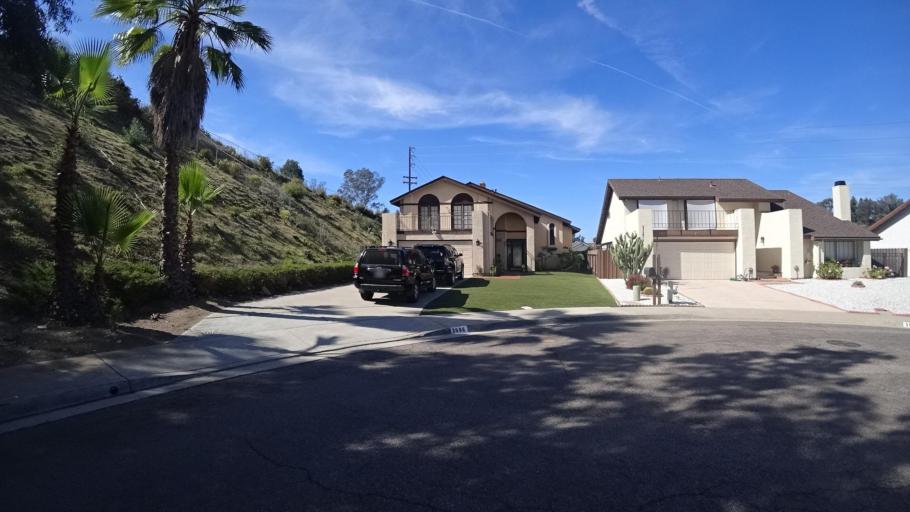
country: US
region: California
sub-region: San Diego County
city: Rancho San Diego
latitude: 32.7506
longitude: -116.9533
